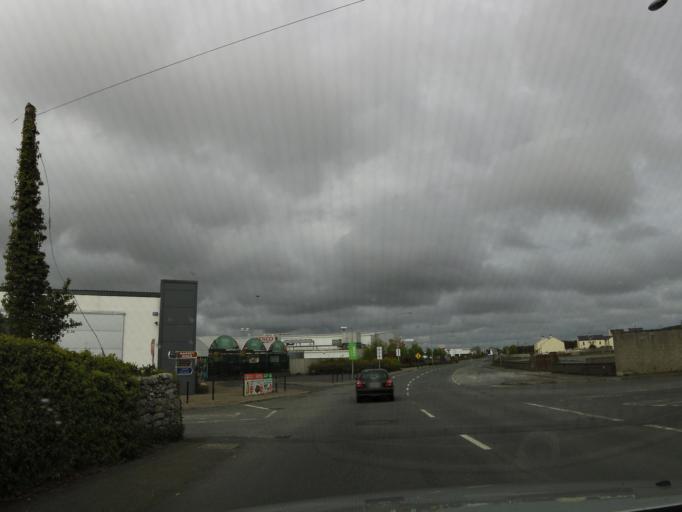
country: IE
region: Connaught
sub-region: Maigh Eo
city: Ballinrobe
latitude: 53.6264
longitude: -9.2187
